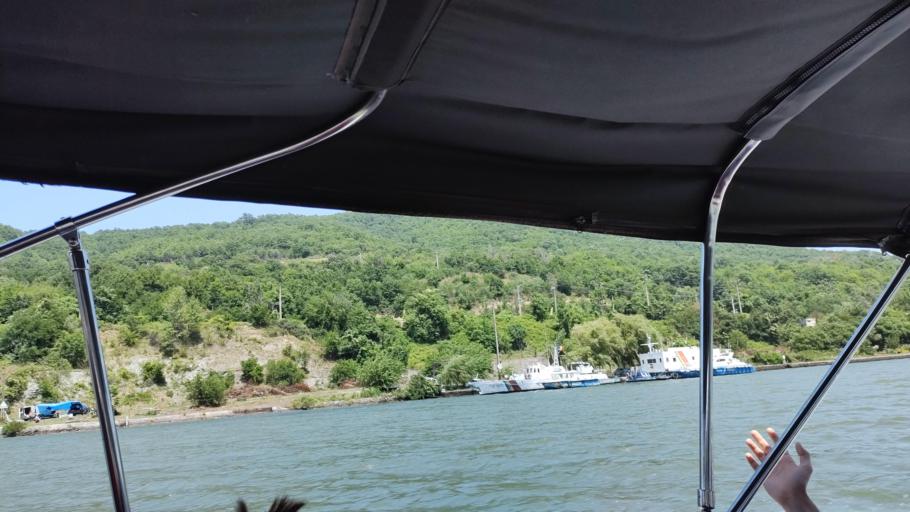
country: RO
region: Caras-Severin
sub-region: Comuna Berzasca
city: Berzasca
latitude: 44.6364
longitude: 21.9636
